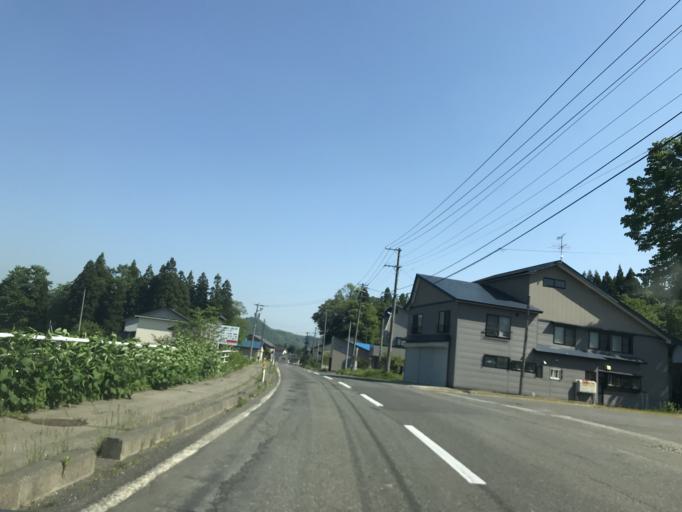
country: JP
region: Akita
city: Yokotemachi
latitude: 39.4107
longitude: 140.7495
